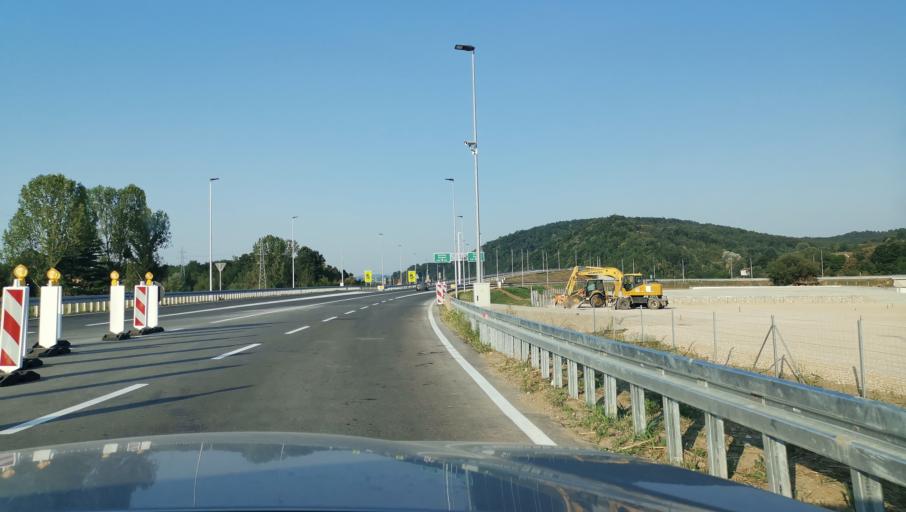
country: RS
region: Central Serbia
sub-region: Kolubarski Okrug
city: Ljig
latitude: 44.2319
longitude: 20.2499
